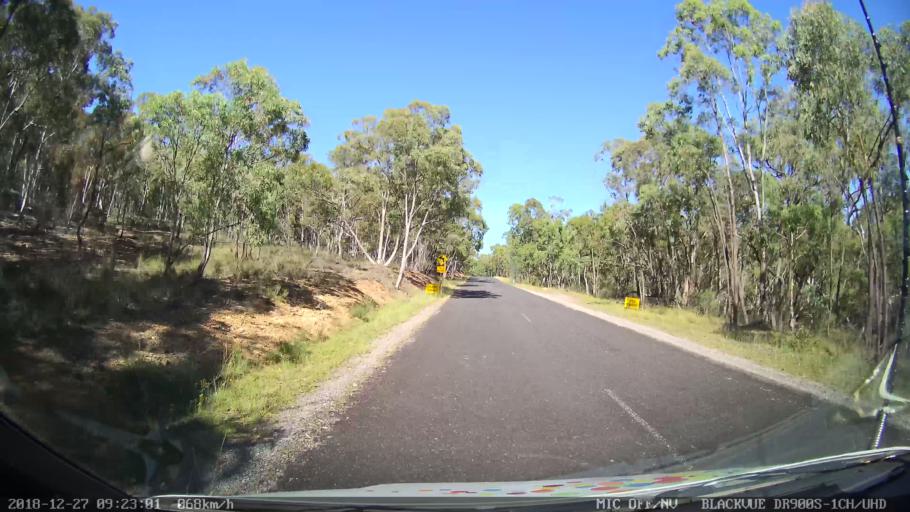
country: AU
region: New South Wales
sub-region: Lithgow
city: Portland
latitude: -33.1239
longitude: 150.0017
